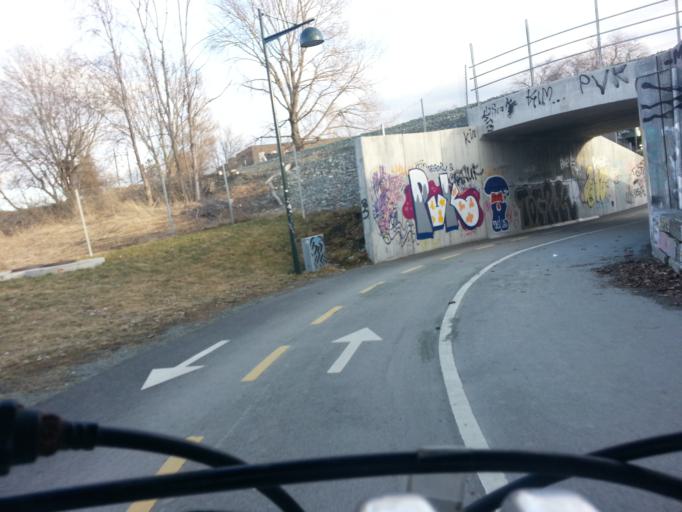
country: NO
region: Sor-Trondelag
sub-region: Trondheim
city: Trondheim
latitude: 63.4403
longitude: 10.4479
